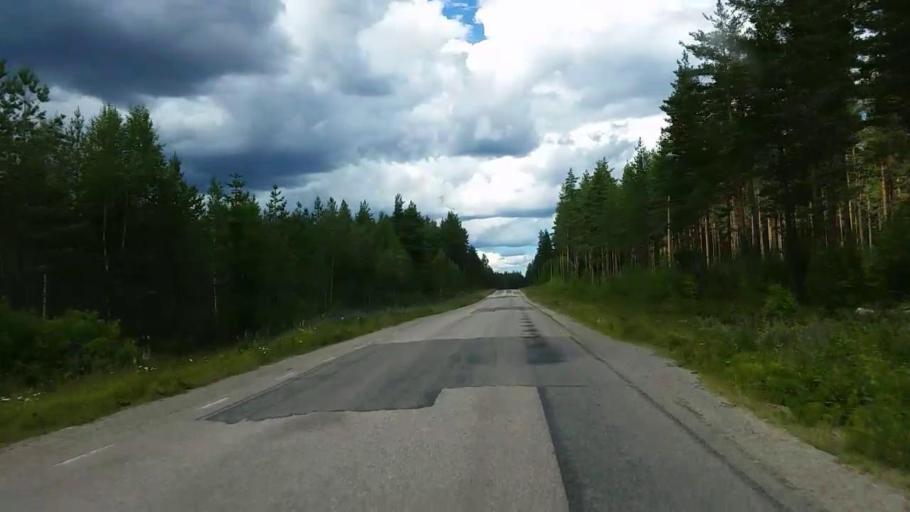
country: SE
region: Gaevleborg
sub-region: Ovanakers Kommun
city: Edsbyn
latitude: 61.4041
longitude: 15.8963
